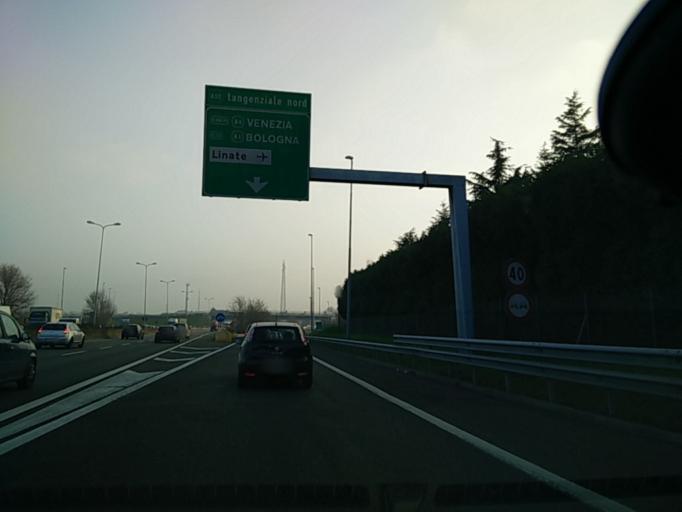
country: IT
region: Lombardy
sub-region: Citta metropolitana di Milano
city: Paderno Dugnano
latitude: 45.5653
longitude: 9.1774
